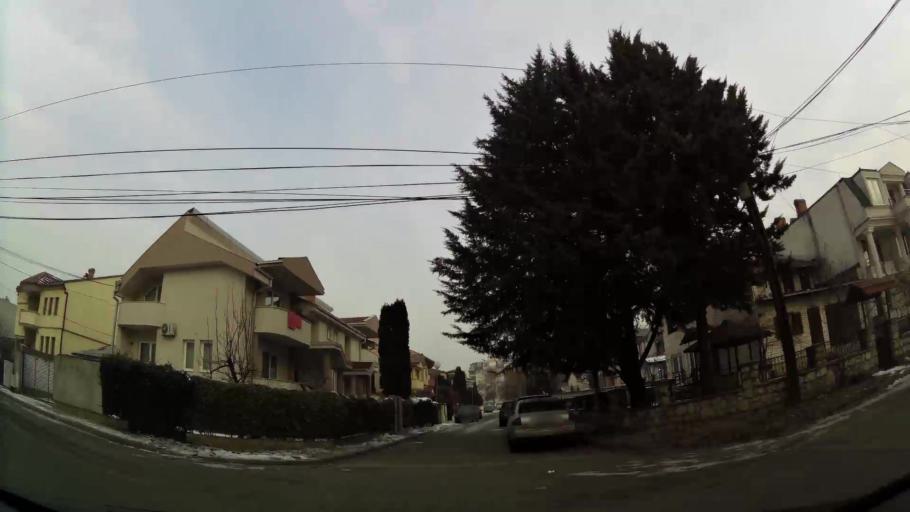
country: MK
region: Butel
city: Butel
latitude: 42.0233
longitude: 21.4482
